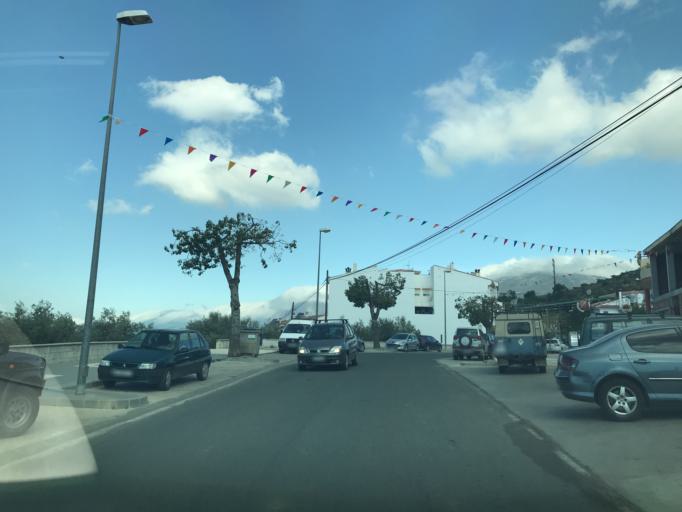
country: ES
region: Andalusia
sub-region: Provincia de Malaga
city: Periana
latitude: 36.9260
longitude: -4.1850
